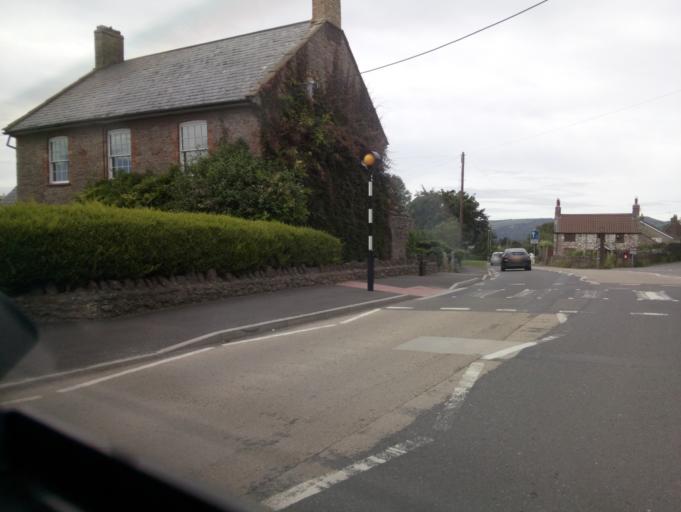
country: GB
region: England
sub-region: Somerset
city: Bradley Cross
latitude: 51.2575
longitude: -2.7522
